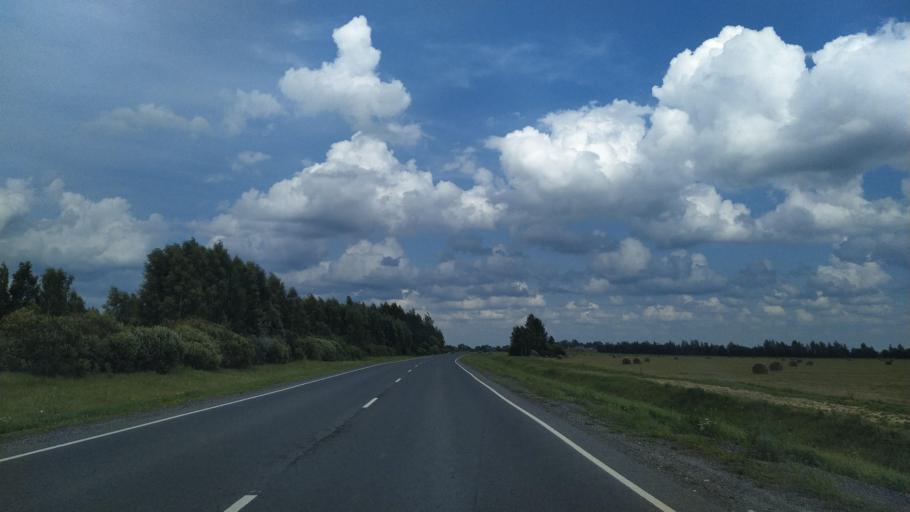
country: RU
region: Novgorod
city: Sol'tsy
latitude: 58.0785
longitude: 30.0757
